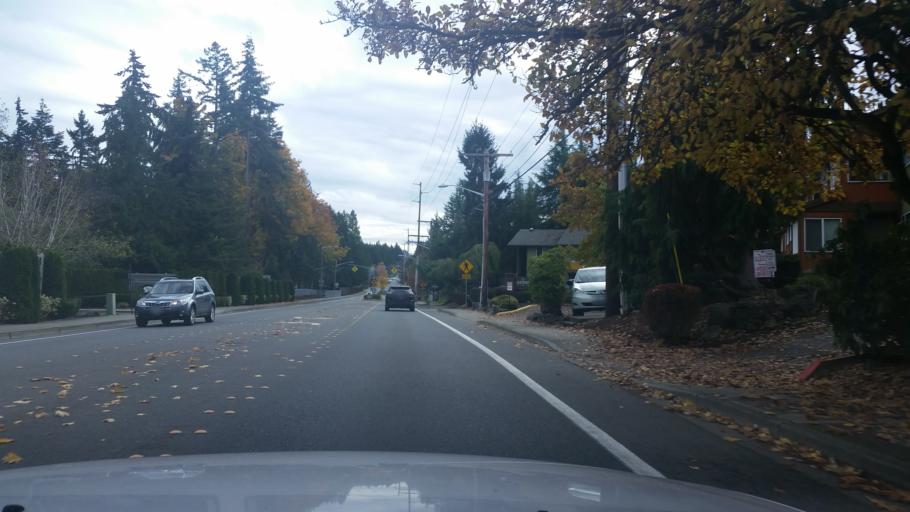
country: US
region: Washington
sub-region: King County
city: Eastgate
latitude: 47.6008
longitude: -122.1532
